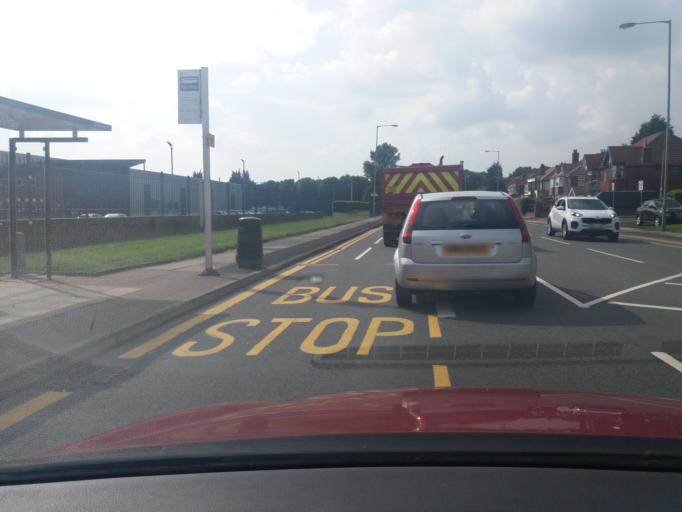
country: GB
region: England
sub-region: Borough of Bolton
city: Horwich
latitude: 53.5853
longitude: -2.5245
